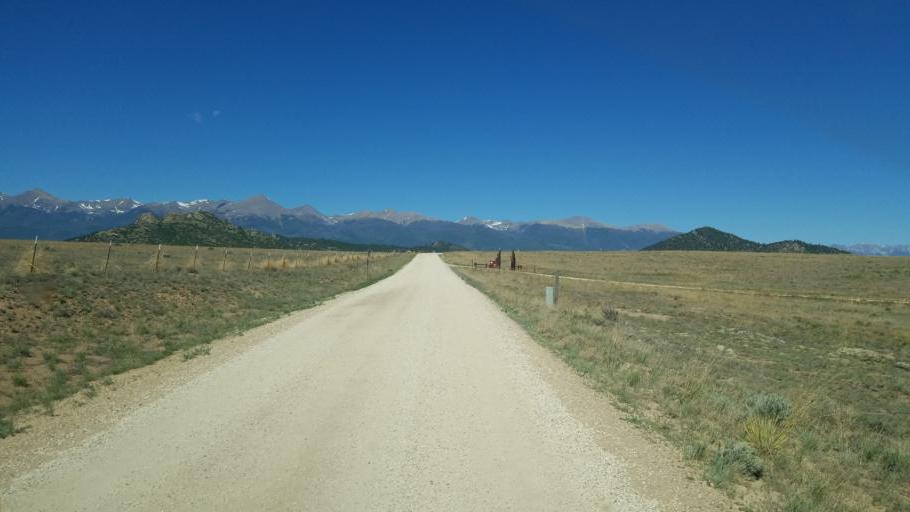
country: US
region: Colorado
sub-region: Custer County
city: Westcliffe
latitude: 38.2357
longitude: -105.4848
